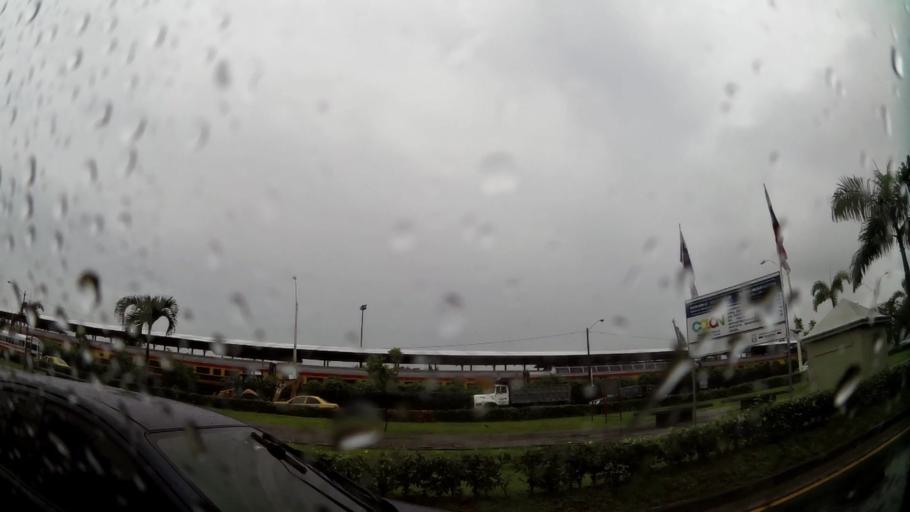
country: PA
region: Colon
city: Colon
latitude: 9.3502
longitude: -79.8993
